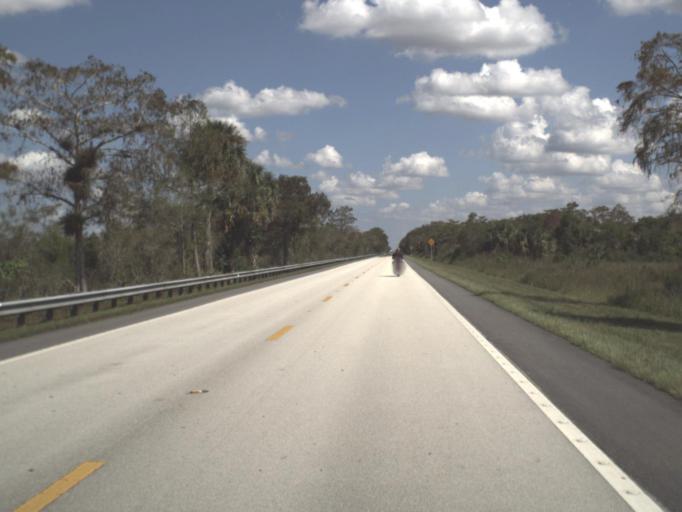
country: US
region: Florida
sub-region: Collier County
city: Lely Resort
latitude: 25.8678
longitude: -81.1409
